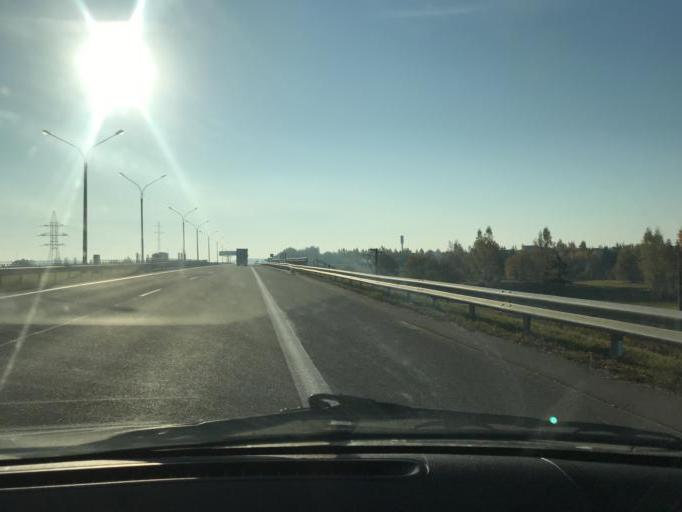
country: BY
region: Minsk
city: Slabada
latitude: 53.9945
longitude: 27.9172
